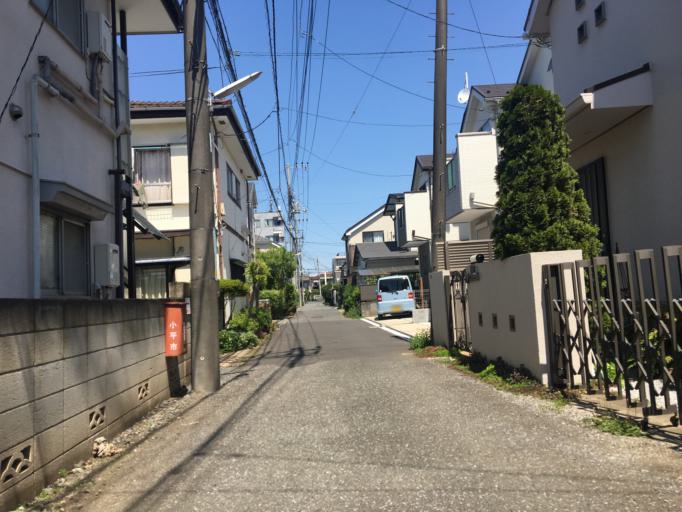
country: JP
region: Tokyo
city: Tanashicho
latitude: 35.7217
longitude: 139.5145
